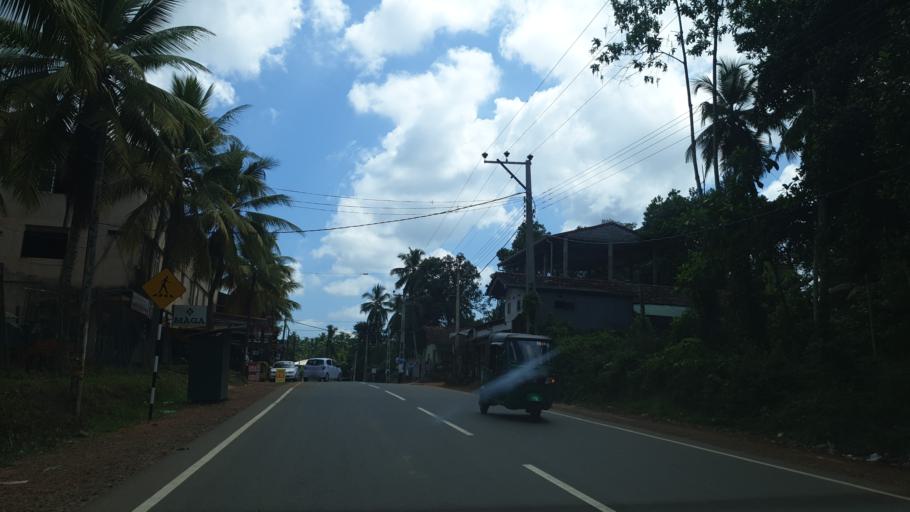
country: LK
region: Western
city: Panadura
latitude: 6.6651
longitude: 79.9506
